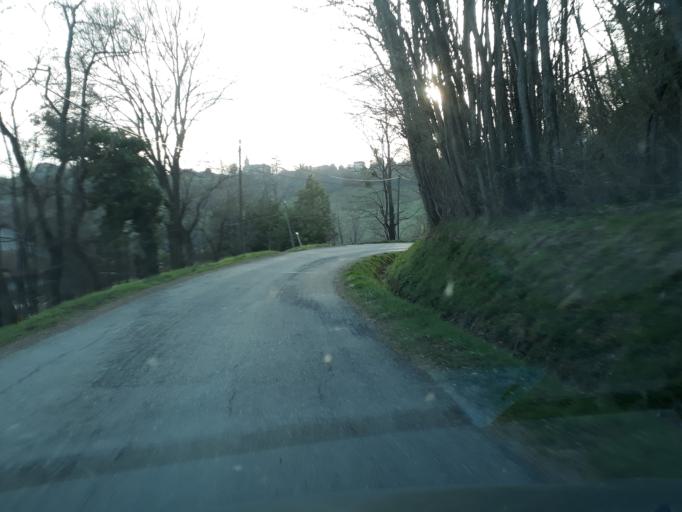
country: FR
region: Midi-Pyrenees
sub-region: Departement de la Haute-Garonne
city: Montesquieu-Volvestre
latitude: 43.1694
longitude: 1.3198
